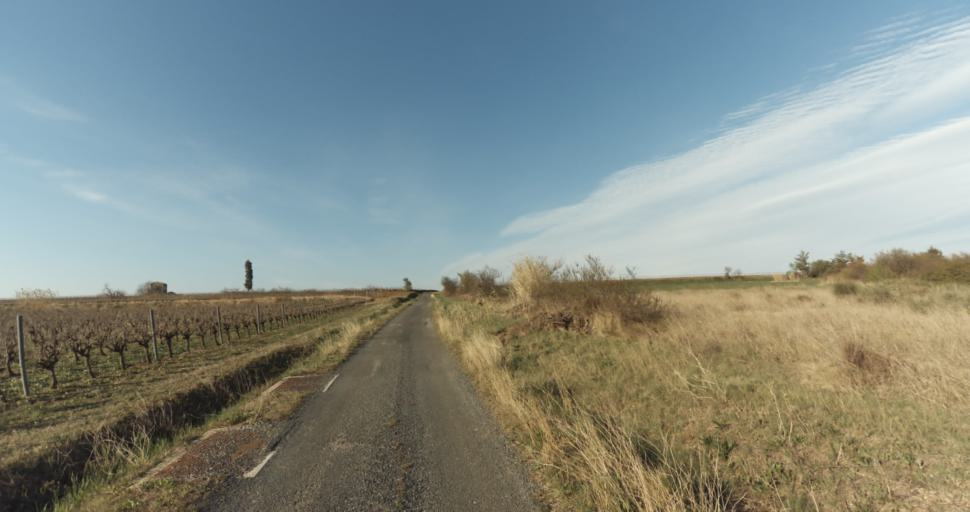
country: FR
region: Languedoc-Roussillon
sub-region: Departement de l'Herault
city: Marseillan
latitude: 43.3803
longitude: 3.5307
